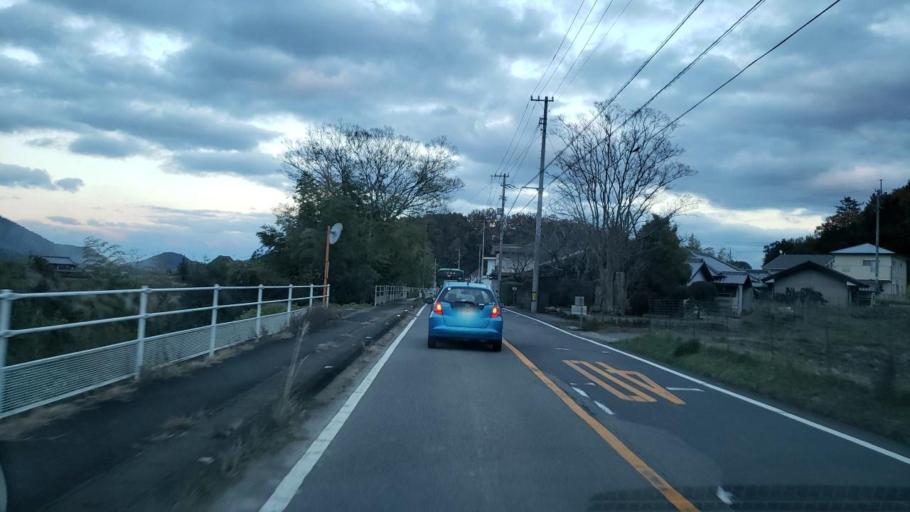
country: JP
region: Tokushima
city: Kamojimacho-jogejima
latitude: 34.2047
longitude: 134.3242
